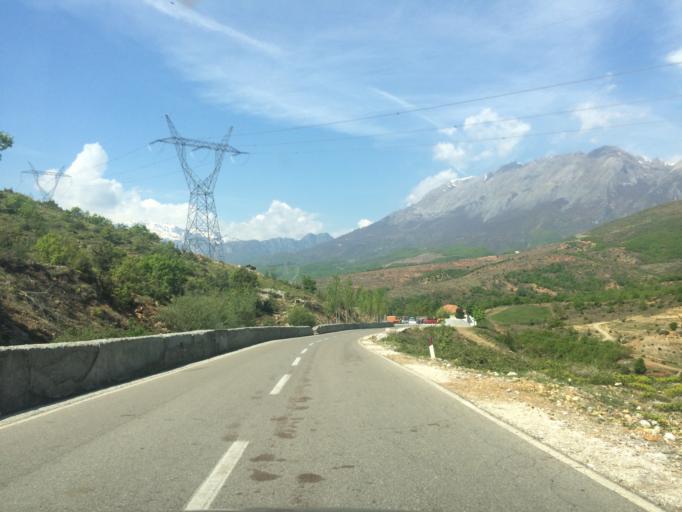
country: AL
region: Kukes
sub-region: Rrethi i Tropojes
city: Bytyc
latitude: 42.4002
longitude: 20.1954
